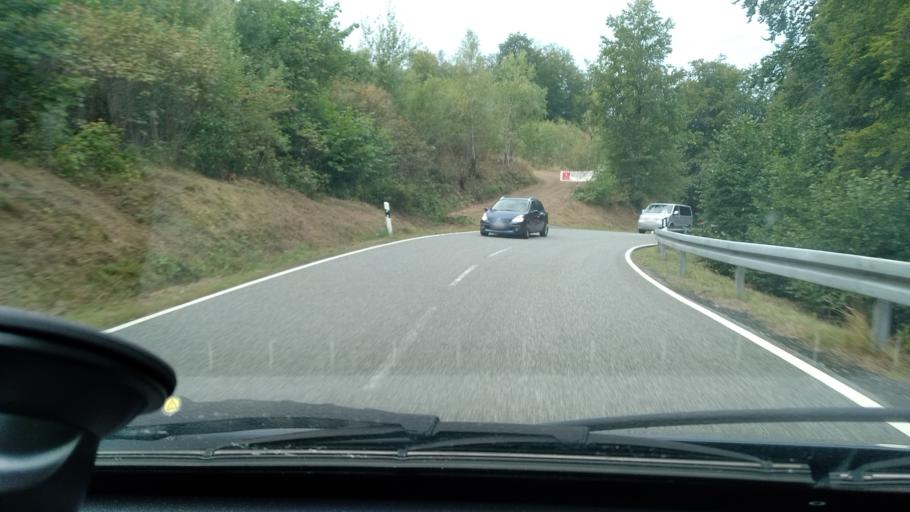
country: DE
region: Hesse
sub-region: Regierungsbezirk Giessen
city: Siegbach
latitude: 50.7902
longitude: 8.3783
